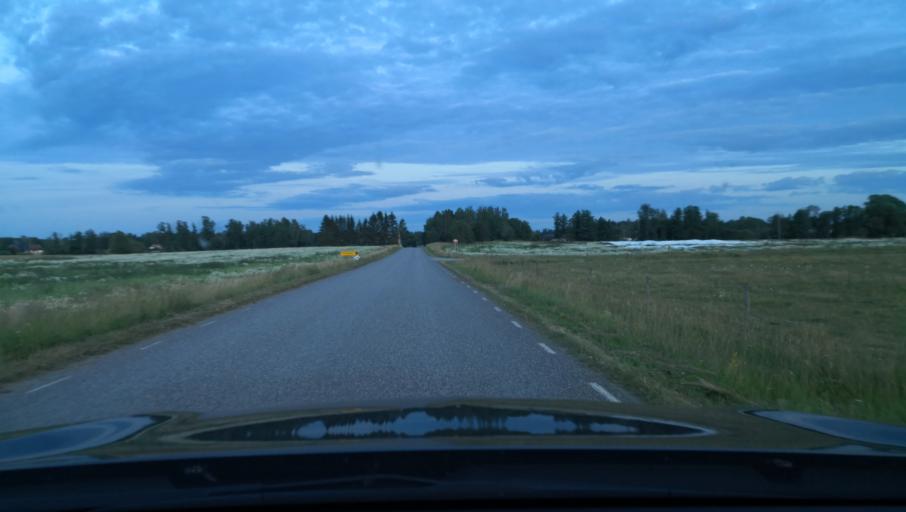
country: SE
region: Uppsala
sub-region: Osthammars Kommun
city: Bjorklinge
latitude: 60.0450
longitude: 17.4982
